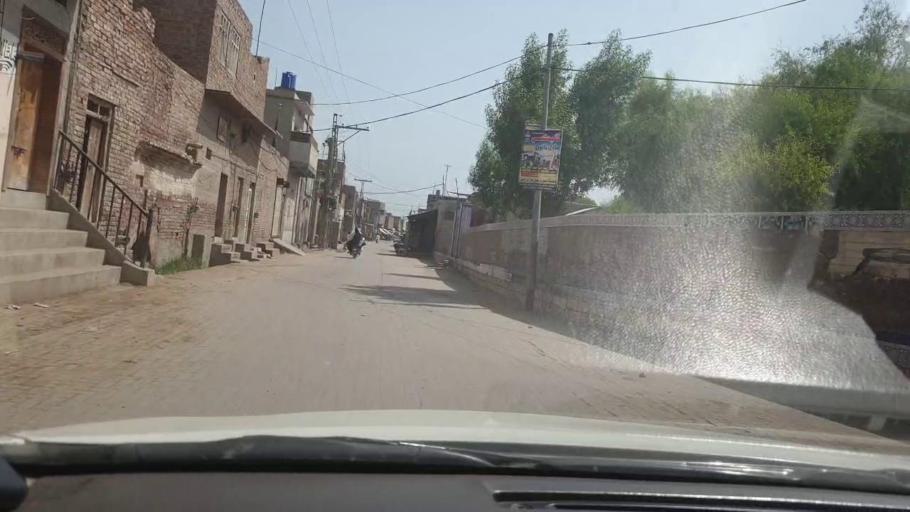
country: PK
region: Sindh
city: Shikarpur
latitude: 27.9499
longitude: 68.6300
